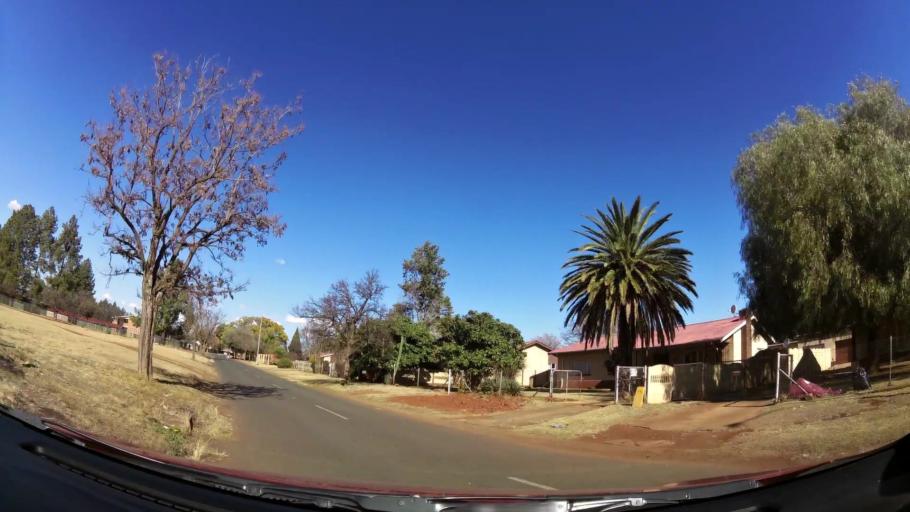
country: ZA
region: Gauteng
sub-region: West Rand District Municipality
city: Carletonville
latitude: -26.3649
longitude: 27.3804
